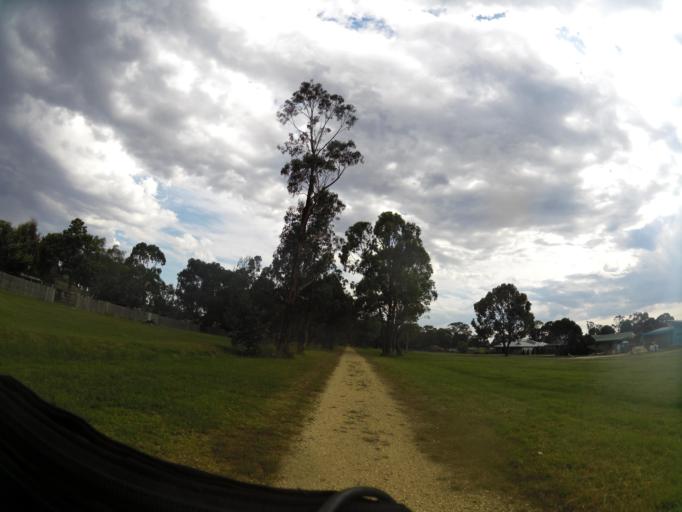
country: AU
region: Victoria
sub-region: Latrobe
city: Traralgon
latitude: -38.0562
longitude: 146.6274
